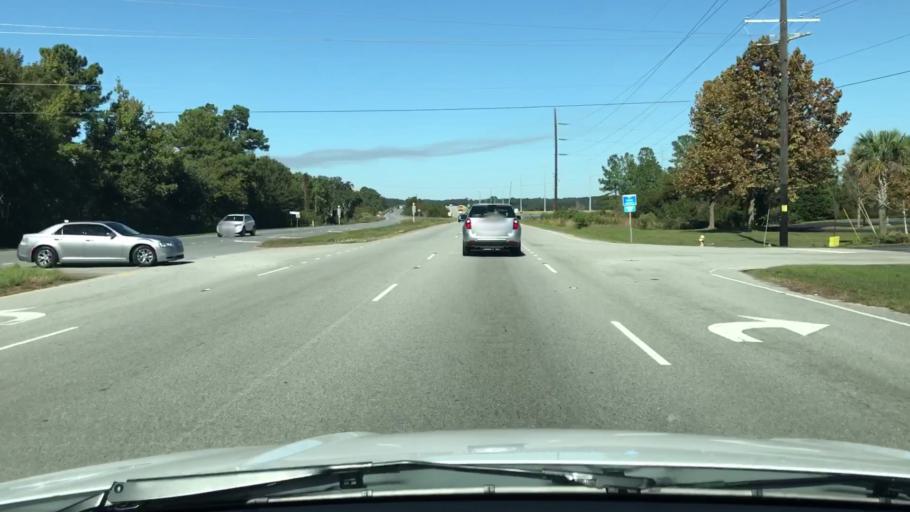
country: US
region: South Carolina
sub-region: Beaufort County
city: Laurel Bay
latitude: 32.5336
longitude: -80.7467
